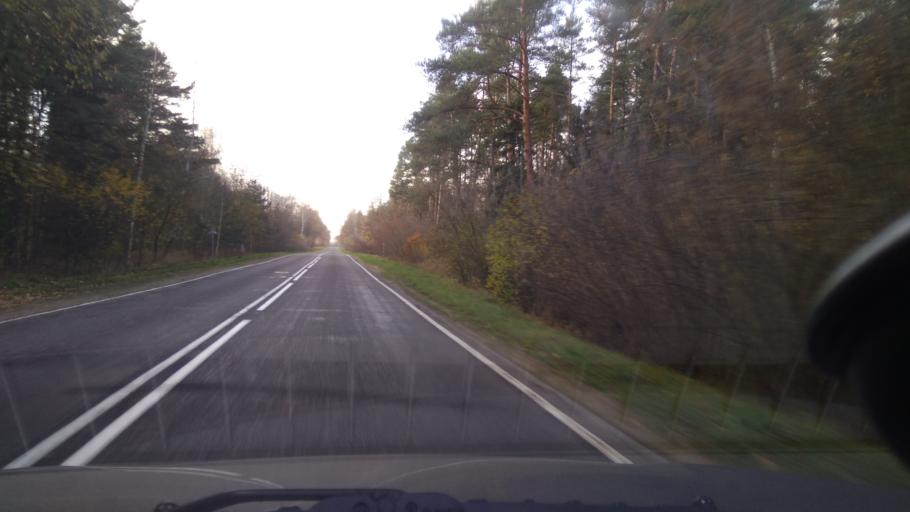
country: BY
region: Minsk
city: Slutsk
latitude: 53.2188
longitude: 27.5744
